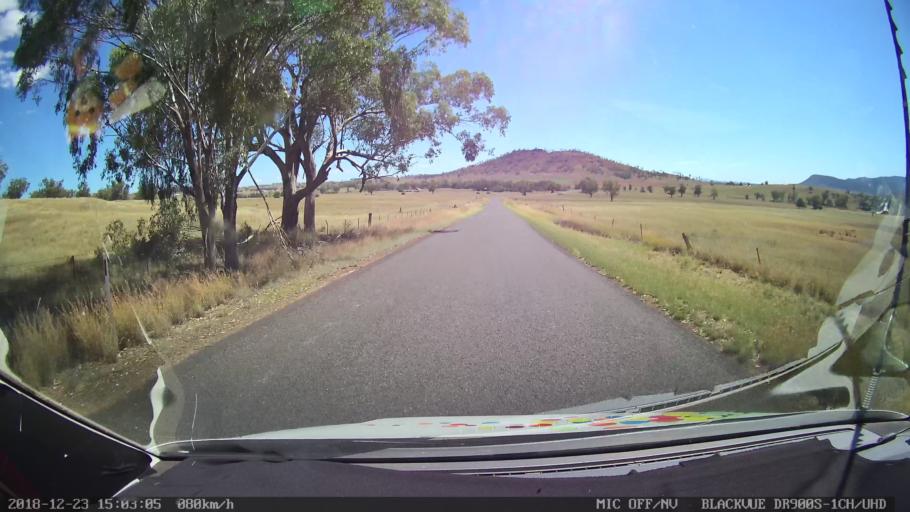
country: AU
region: New South Wales
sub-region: Tamworth Municipality
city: Manilla
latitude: -30.7351
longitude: 150.7686
